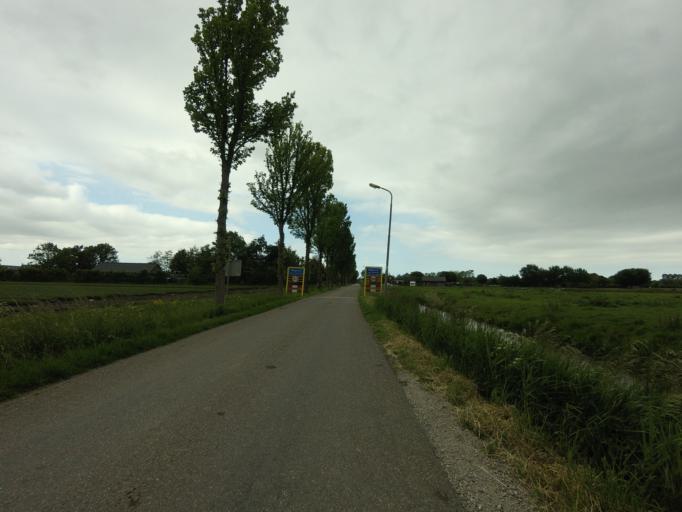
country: NL
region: North Holland
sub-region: Gemeente Hoorn
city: Hoorn
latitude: 52.6733
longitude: 5.0236
